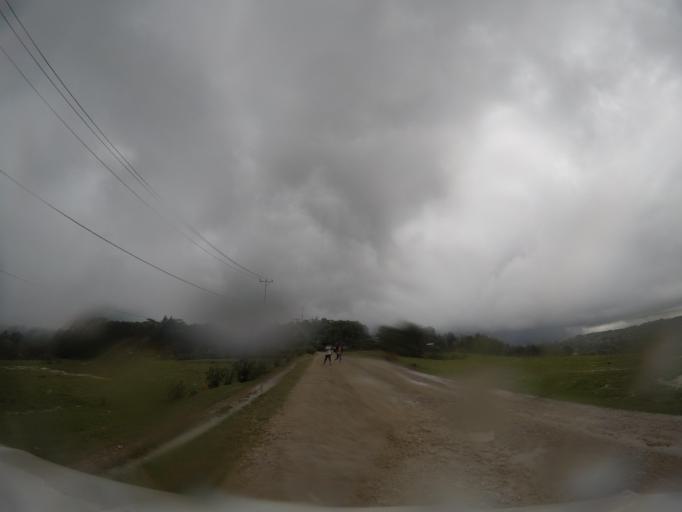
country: TL
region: Baucau
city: Venilale
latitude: -8.6401
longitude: 126.3873
